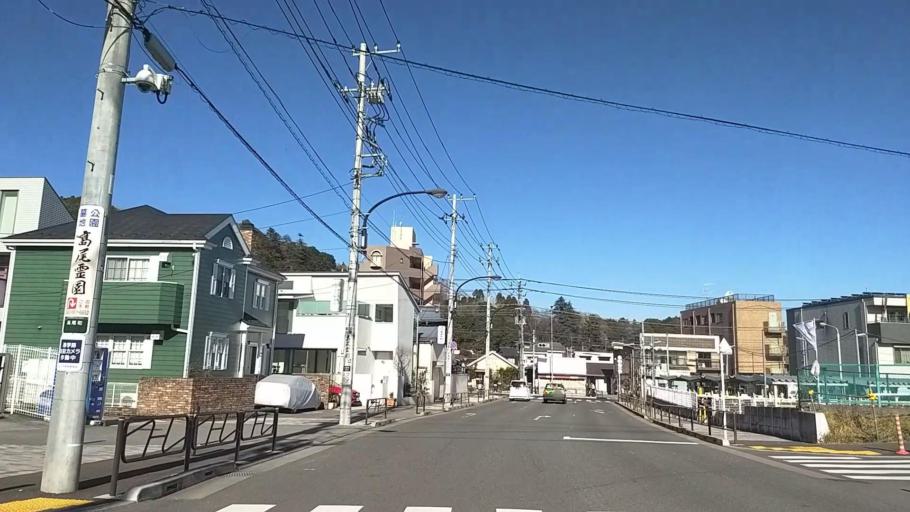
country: JP
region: Tokyo
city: Hachioji
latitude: 35.6417
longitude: 139.2800
